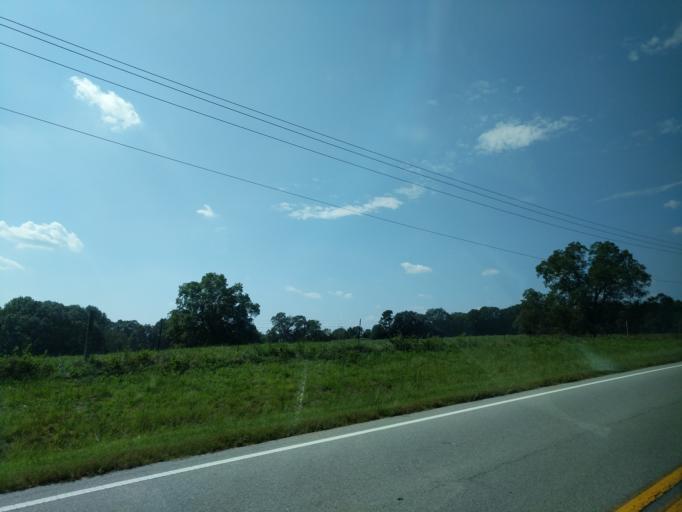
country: US
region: Georgia
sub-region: Franklin County
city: Gumlog
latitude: 34.4620
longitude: -83.0565
